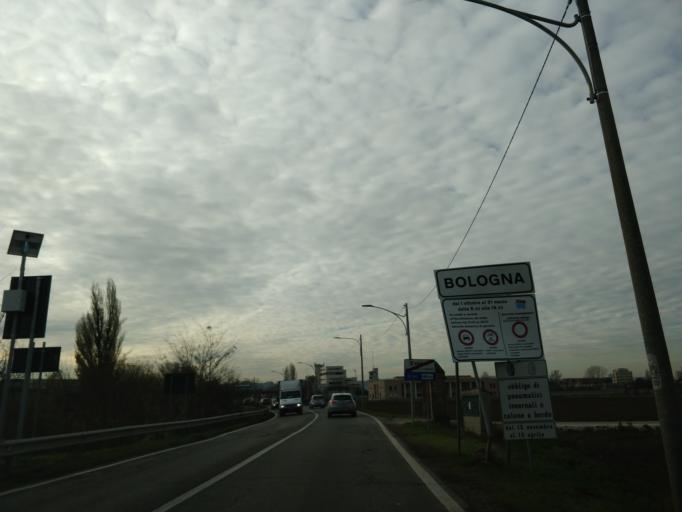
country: IT
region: Emilia-Romagna
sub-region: Provincia di Bologna
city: Progresso
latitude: 44.5392
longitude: 11.3707
